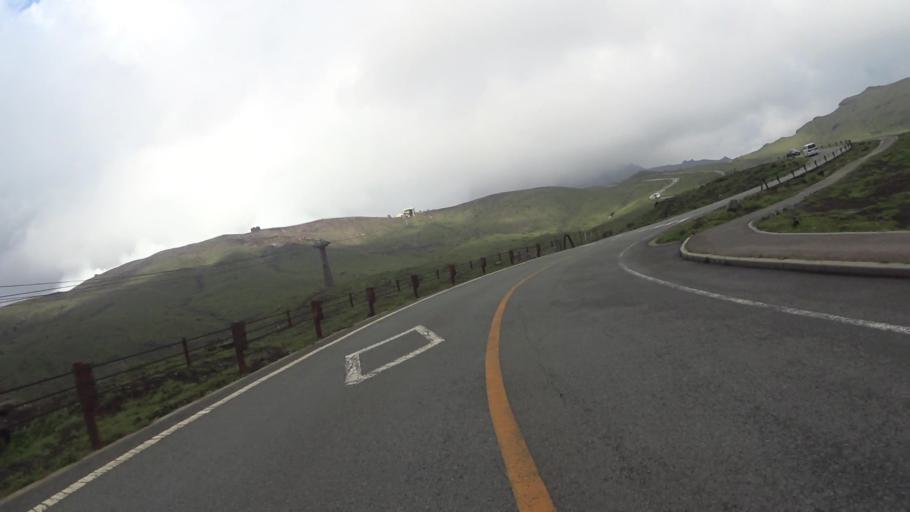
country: JP
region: Kumamoto
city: Aso
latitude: 32.8796
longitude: 131.0769
